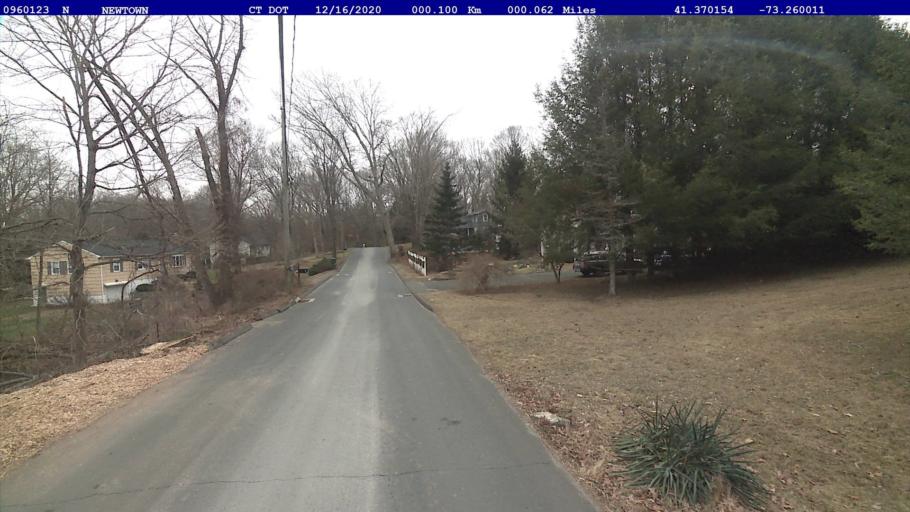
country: US
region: Connecticut
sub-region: Fairfield County
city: Newtown
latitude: 41.3702
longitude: -73.2600
